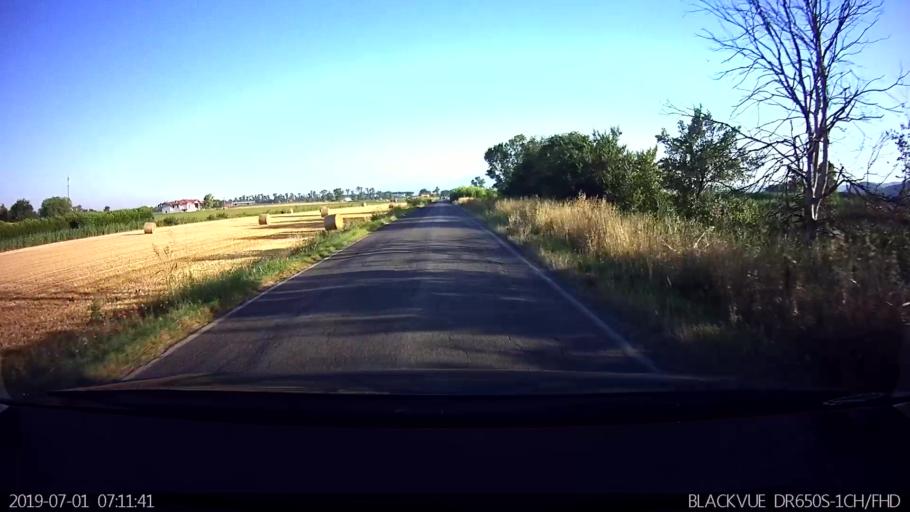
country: IT
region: Latium
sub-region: Provincia di Latina
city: Borgo Hermada
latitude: 41.3224
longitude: 13.1771
